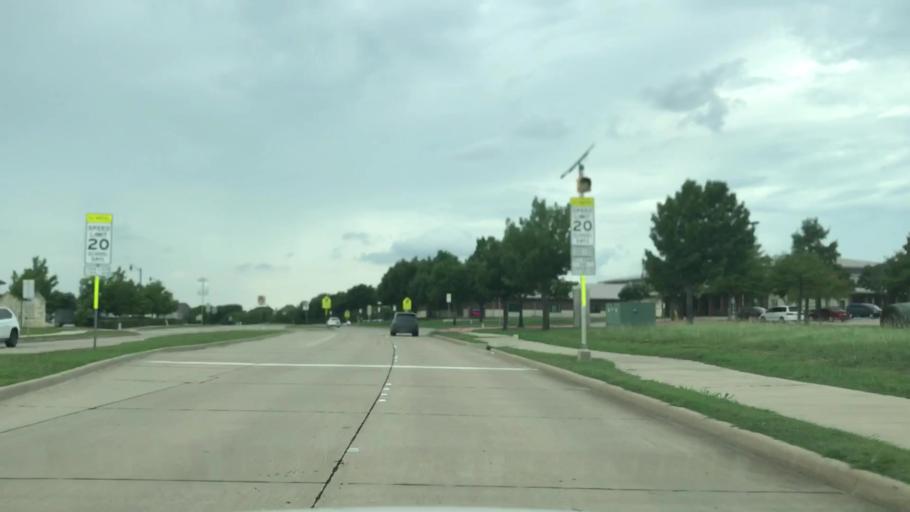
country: US
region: Texas
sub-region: Collin County
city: Frisco
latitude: 33.1294
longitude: -96.8086
